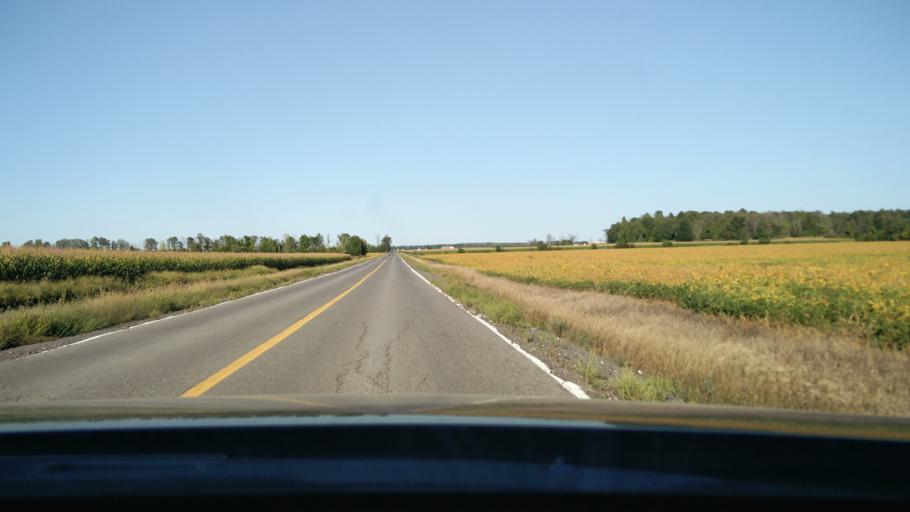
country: CA
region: Ontario
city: Bells Corners
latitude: 45.2014
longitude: -75.8088
